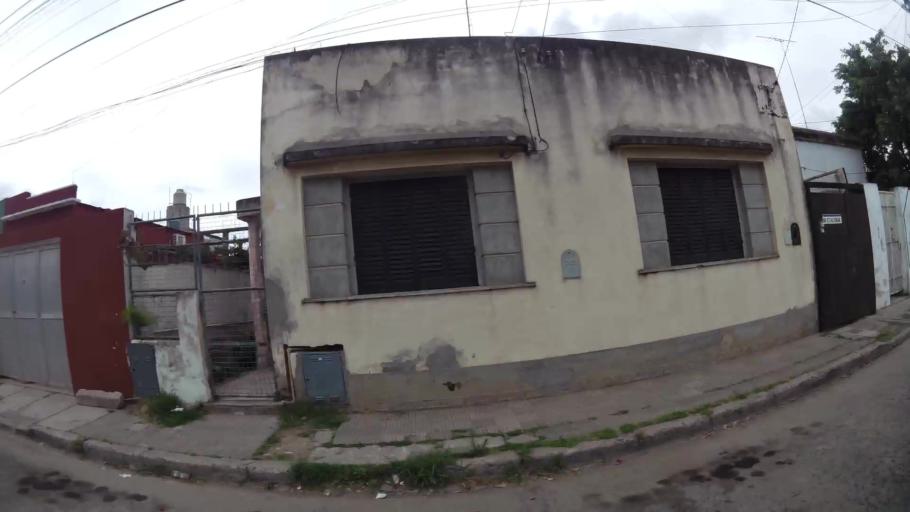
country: AR
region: Buenos Aires
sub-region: Partido de Zarate
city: Zarate
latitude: -34.1079
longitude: -59.0135
